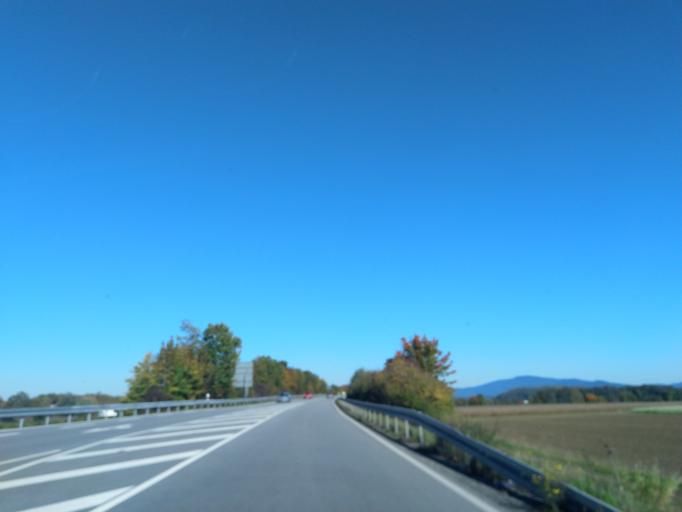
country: DE
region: Bavaria
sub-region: Lower Bavaria
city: Plattling
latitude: 48.7995
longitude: 12.9040
